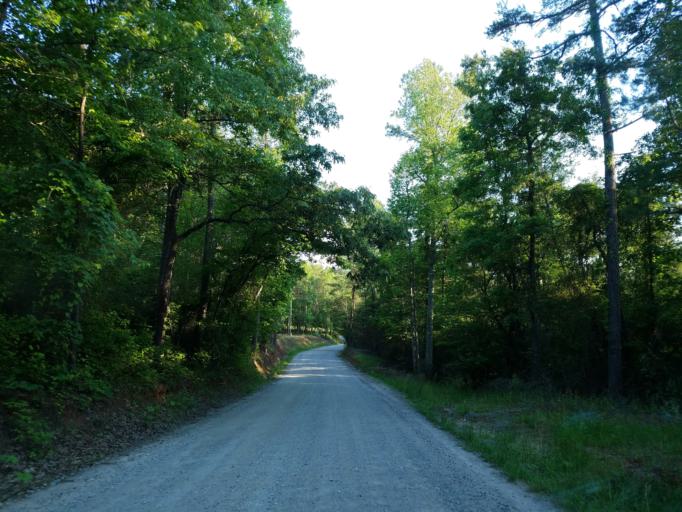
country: US
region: Georgia
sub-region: Cherokee County
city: Ball Ground
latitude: 34.3456
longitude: -84.3249
